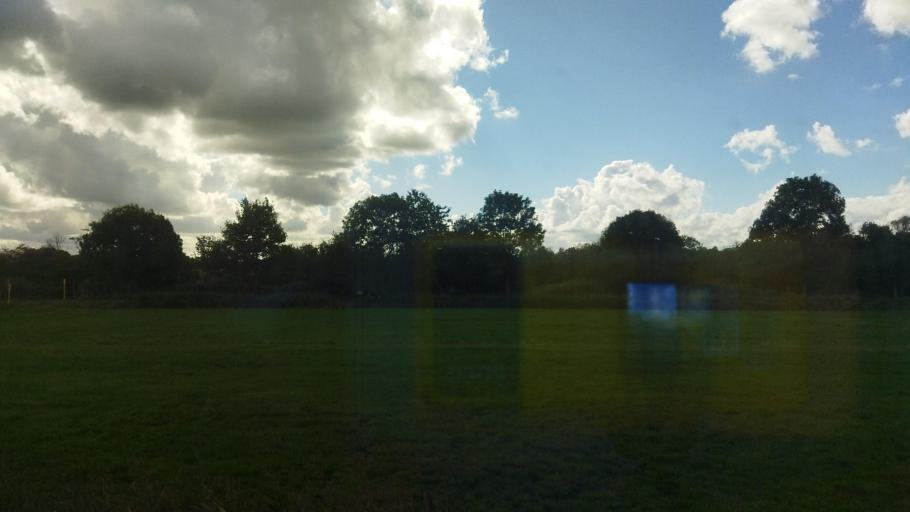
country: DE
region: Lower Saxony
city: Emden
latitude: 53.3392
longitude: 7.2815
